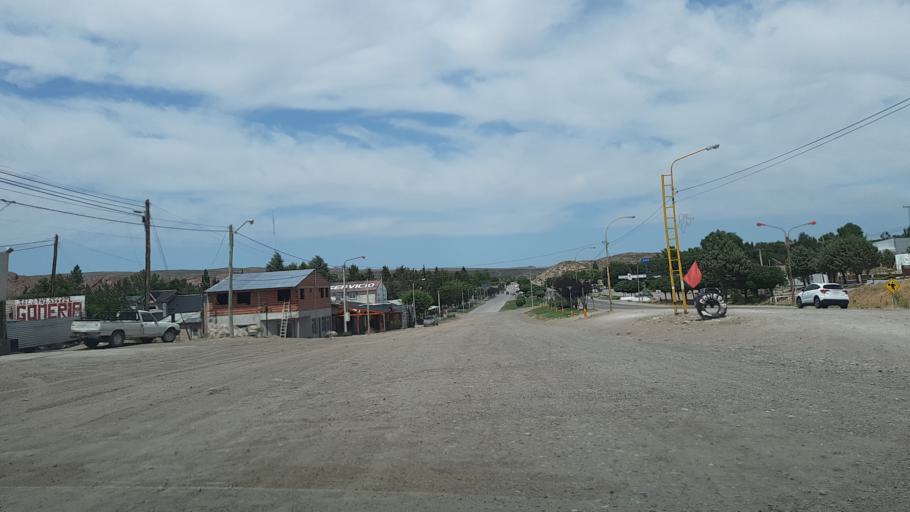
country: AR
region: Neuquen
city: Piedra del Aguila
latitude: -40.0465
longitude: -70.0738
